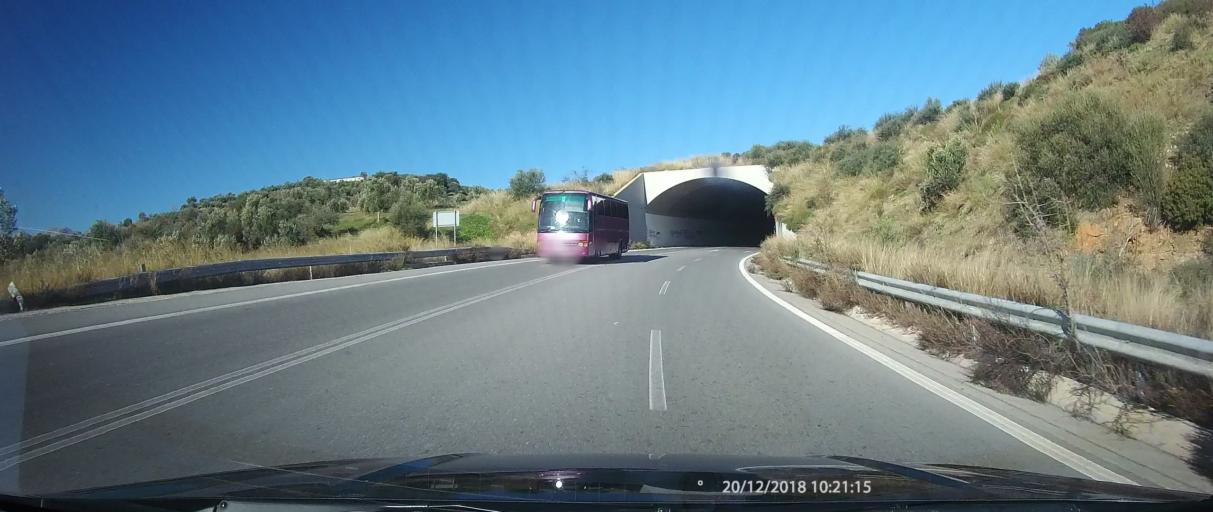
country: GR
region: Peloponnese
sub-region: Nomos Lakonias
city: Magoula
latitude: 37.1571
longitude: 22.4265
